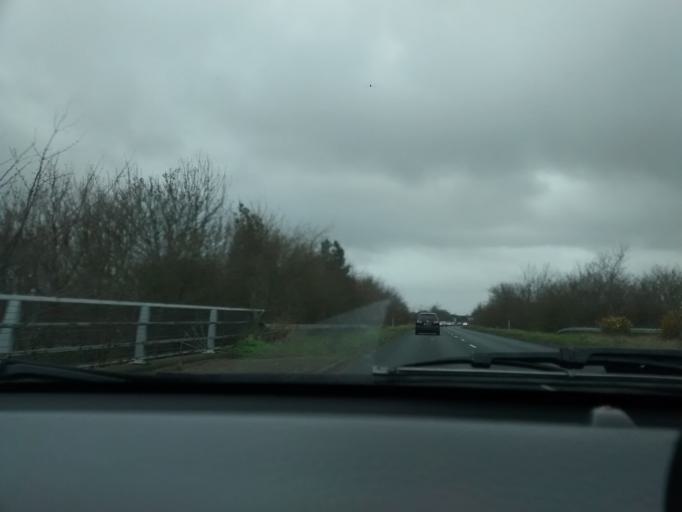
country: GB
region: England
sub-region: Suffolk
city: Felixstowe
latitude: 51.9750
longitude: 1.3407
